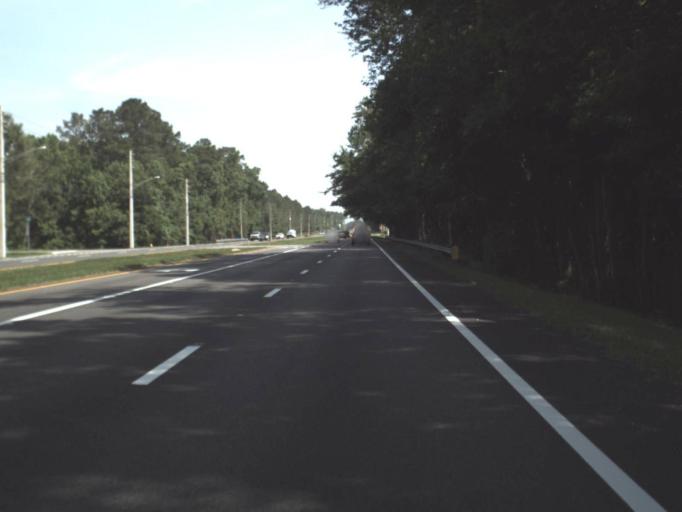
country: US
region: Florida
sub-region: Saint Johns County
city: Fruit Cove
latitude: 30.1534
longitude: -81.5275
